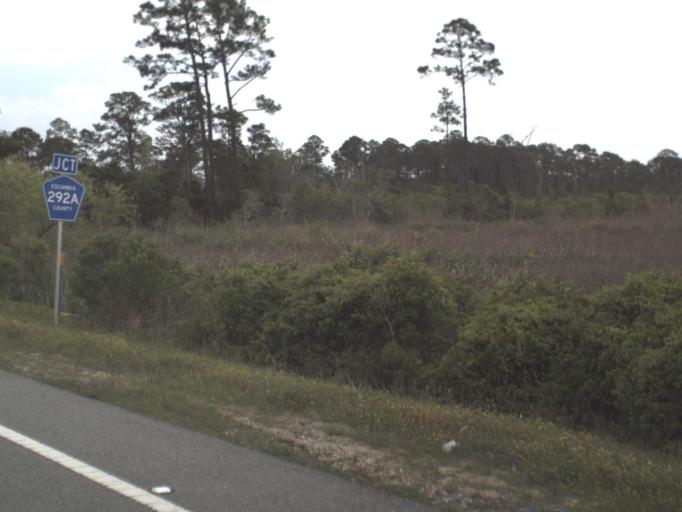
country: US
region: Alabama
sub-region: Baldwin County
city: Orange Beach
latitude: 30.3171
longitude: -87.4249
